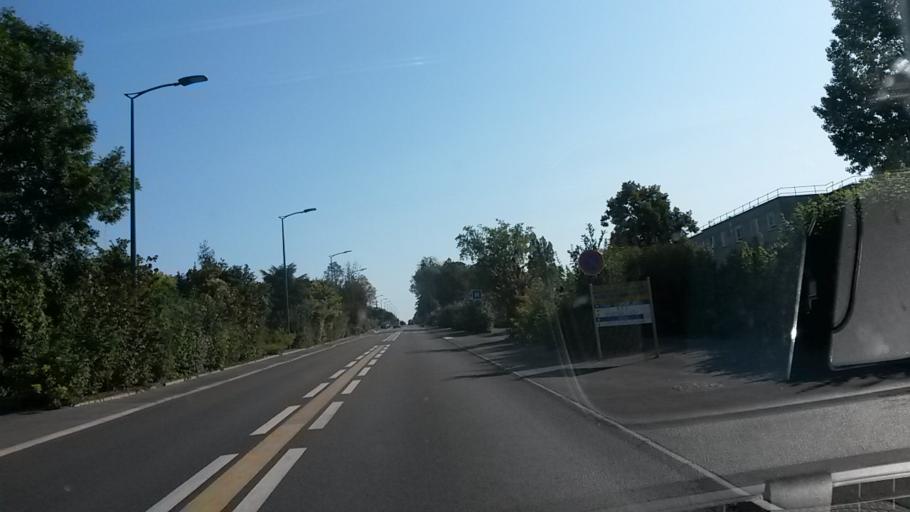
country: FR
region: Picardie
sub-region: Departement de l'Aisne
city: Guise
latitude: 49.9022
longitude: 3.6376
